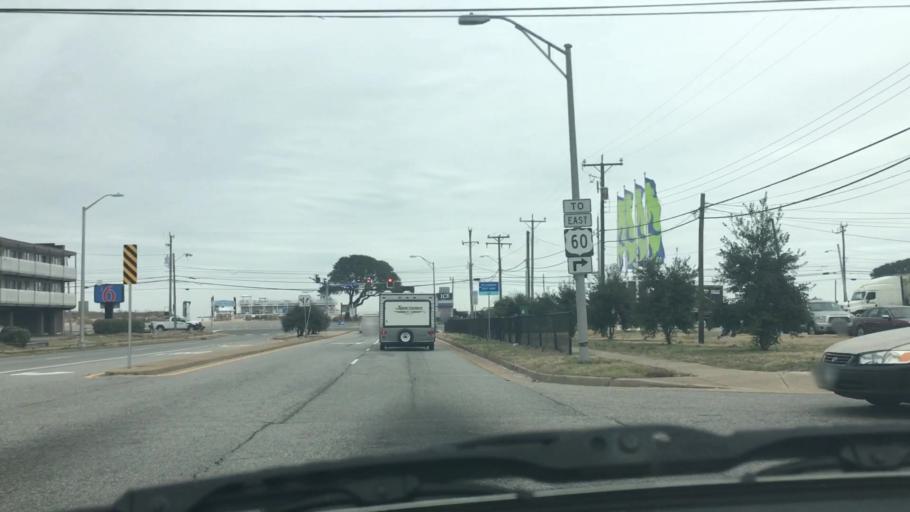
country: US
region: Virginia
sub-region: City of Hampton
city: East Hampton
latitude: 36.9590
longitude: -76.2618
